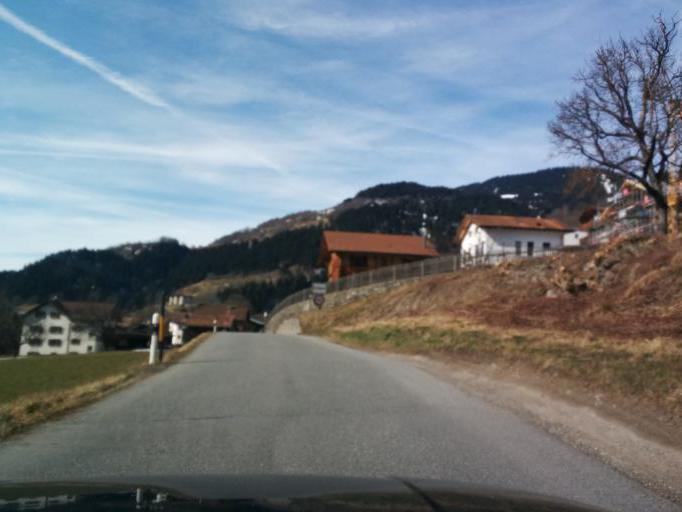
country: CH
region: Grisons
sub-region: Surselva District
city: Laax
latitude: 46.7890
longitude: 9.2365
